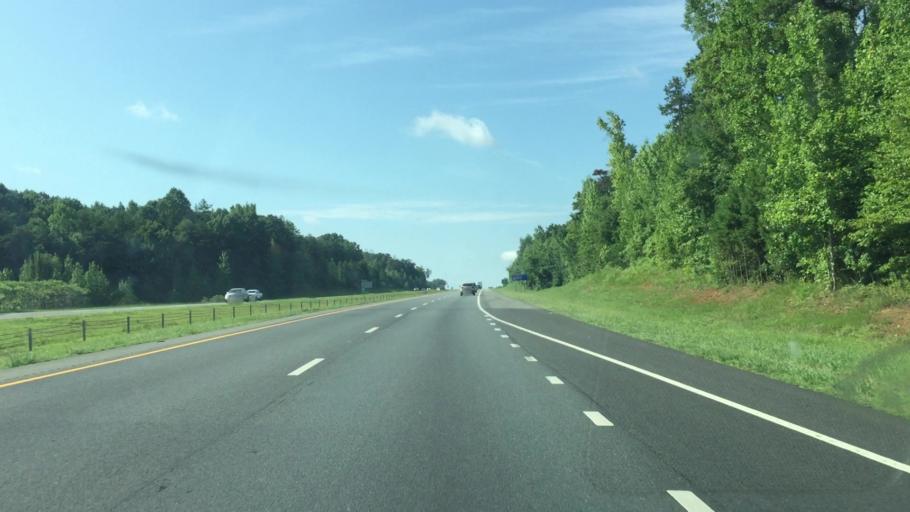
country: US
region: North Carolina
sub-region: Mecklenburg County
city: Mint Hill
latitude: 35.1951
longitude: -80.6294
